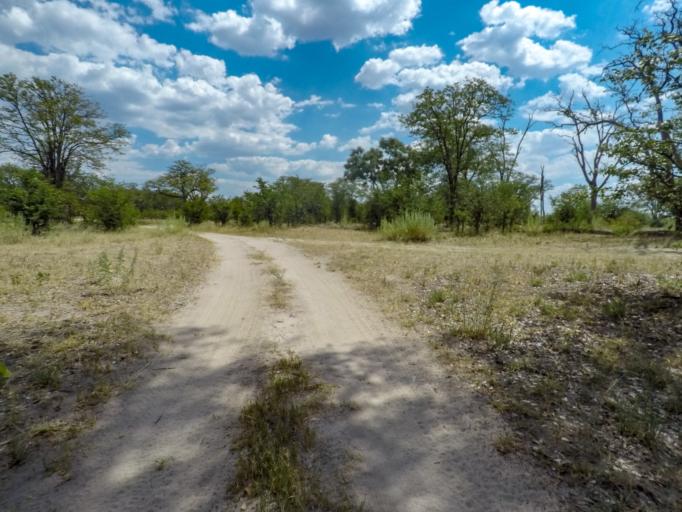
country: BW
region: North West
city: Maun
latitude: -19.2141
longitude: 23.6200
